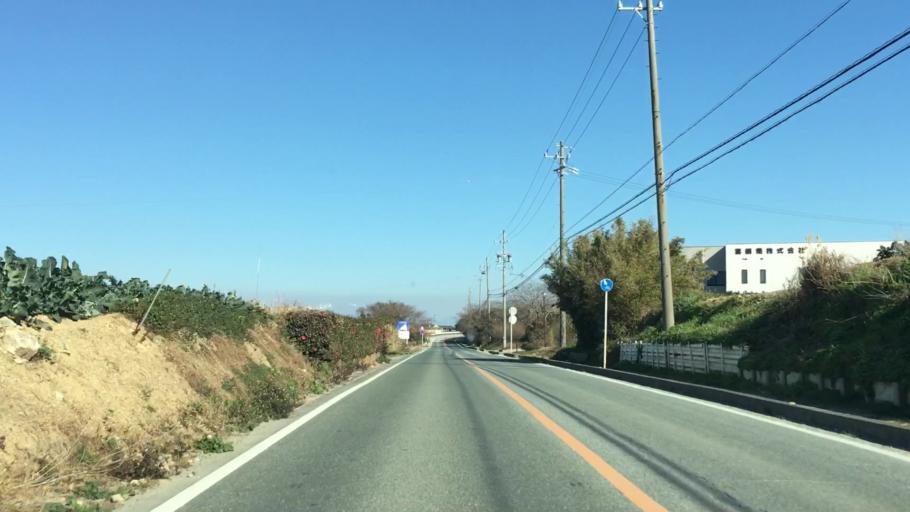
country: JP
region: Aichi
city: Tahara
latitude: 34.6903
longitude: 137.2551
